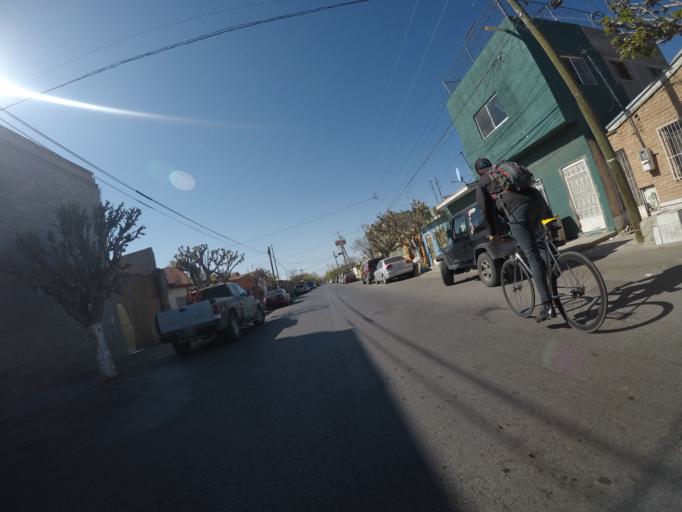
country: MX
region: Chihuahua
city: Ciudad Juarez
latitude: 31.7469
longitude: -106.4732
